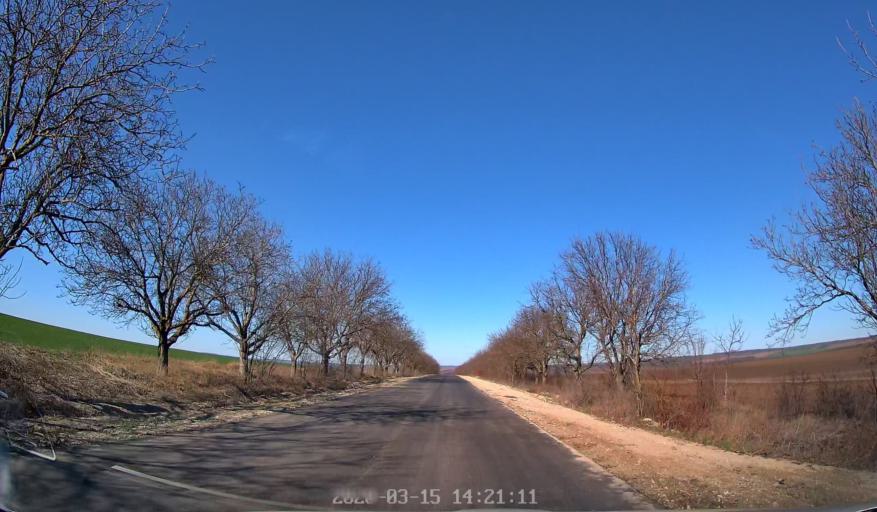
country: MD
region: Orhei
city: Orhei
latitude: 47.3152
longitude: 28.9250
